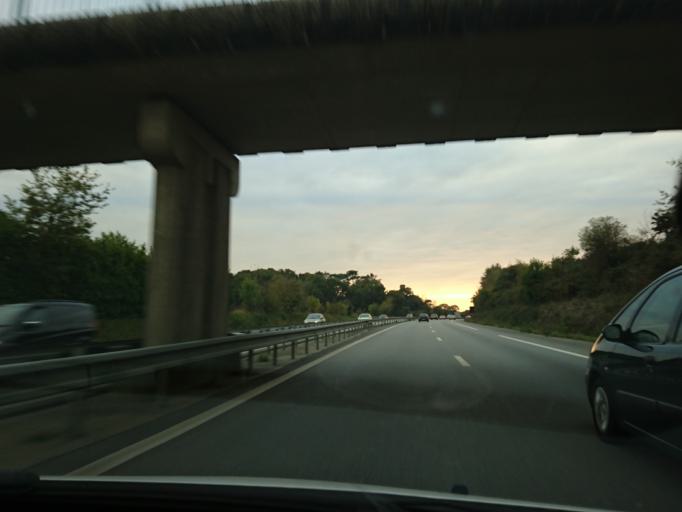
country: FR
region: Brittany
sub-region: Departement du Morbihan
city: Pluneret
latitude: 47.6628
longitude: -2.9628
